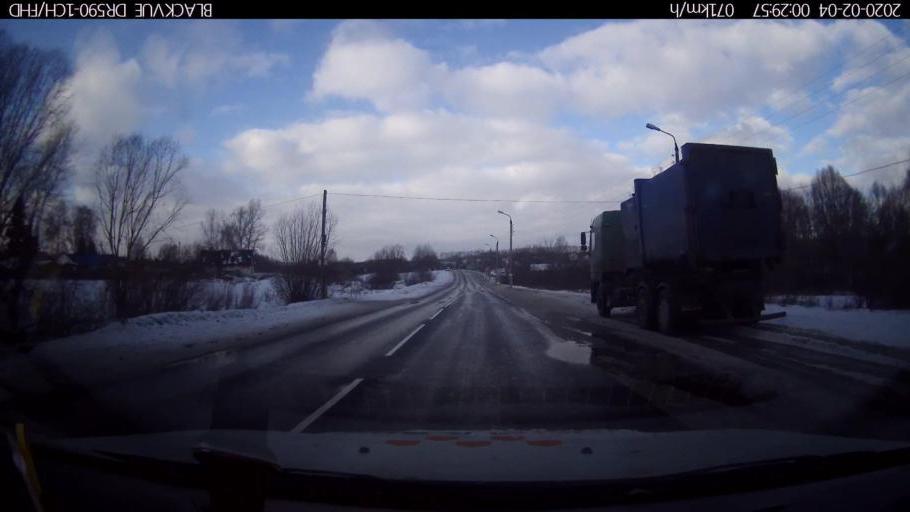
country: RU
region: Nizjnij Novgorod
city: Kstovo
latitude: 56.0359
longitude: 44.1620
